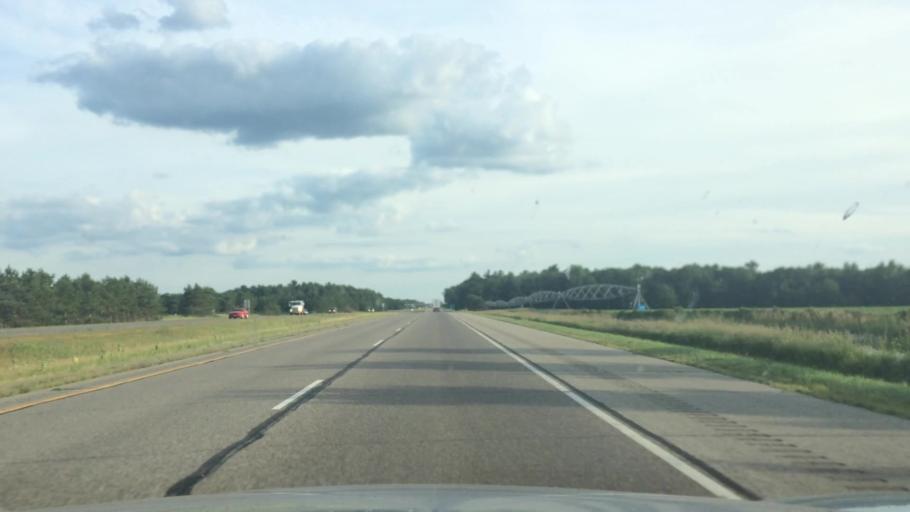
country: US
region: Wisconsin
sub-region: Portage County
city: Plover
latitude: 44.2701
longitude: -89.5239
